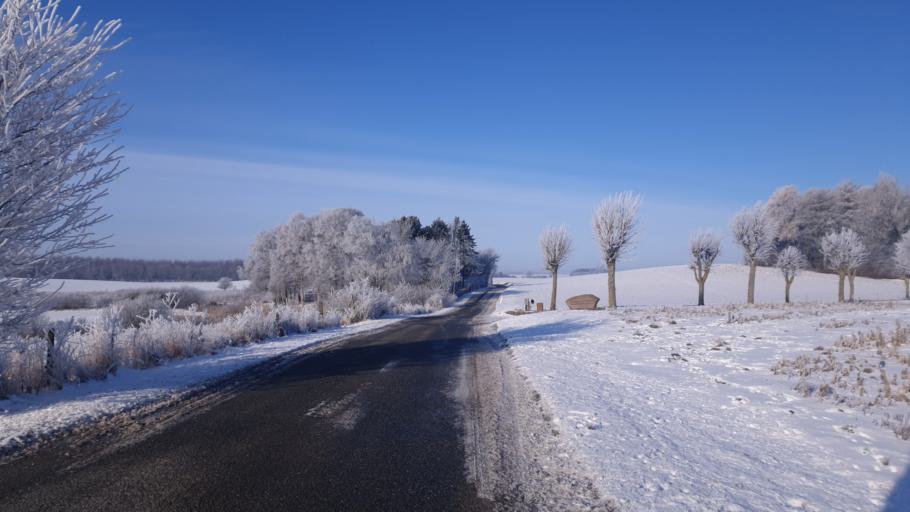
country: DK
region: Central Jutland
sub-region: Hedensted Kommune
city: Hedensted
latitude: 55.8034
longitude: 9.7443
